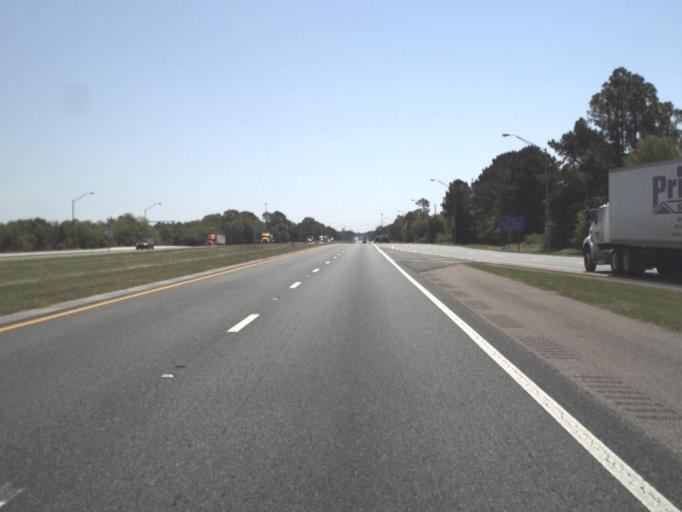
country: US
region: Florida
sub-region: Escambia County
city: Cantonment
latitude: 30.5523
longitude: -87.3609
